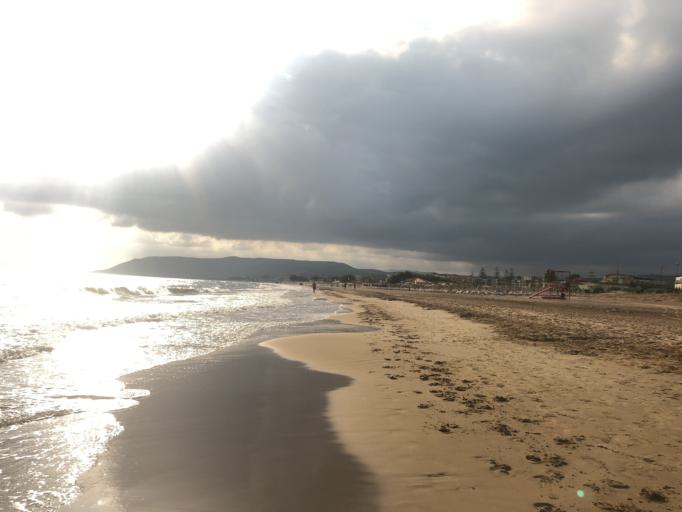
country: GR
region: Crete
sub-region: Nomos Chanias
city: Georgioupolis
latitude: 35.3547
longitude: 24.2917
